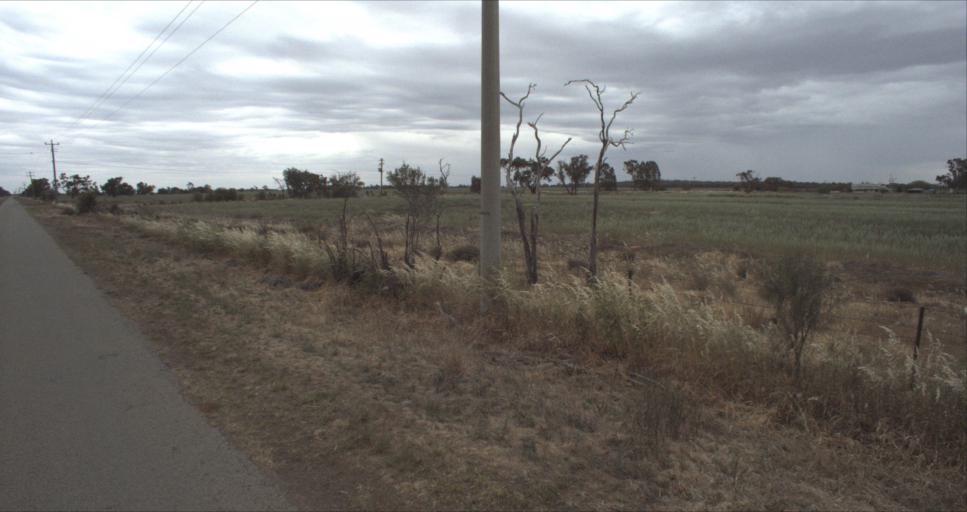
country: AU
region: New South Wales
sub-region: Leeton
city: Leeton
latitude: -34.4134
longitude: 146.3399
